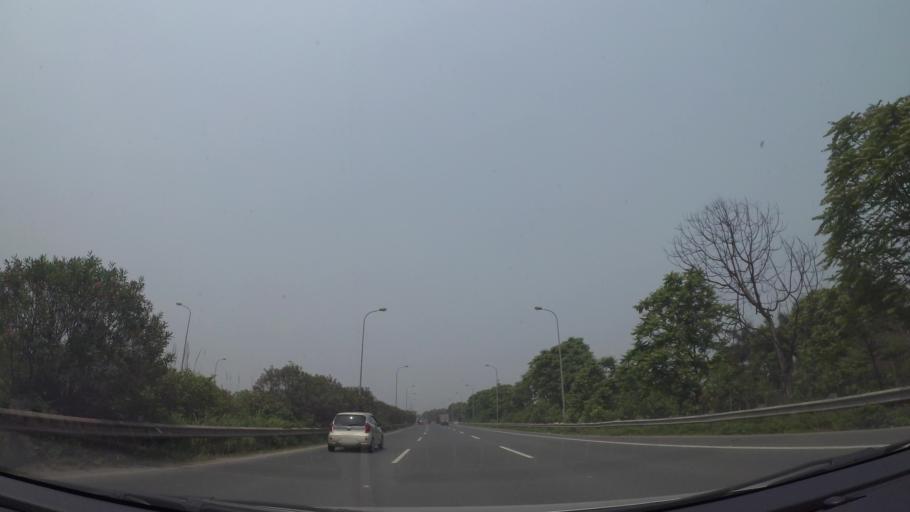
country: VN
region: Ha Noi
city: Cau Dien
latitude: 21.0111
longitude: 105.7158
